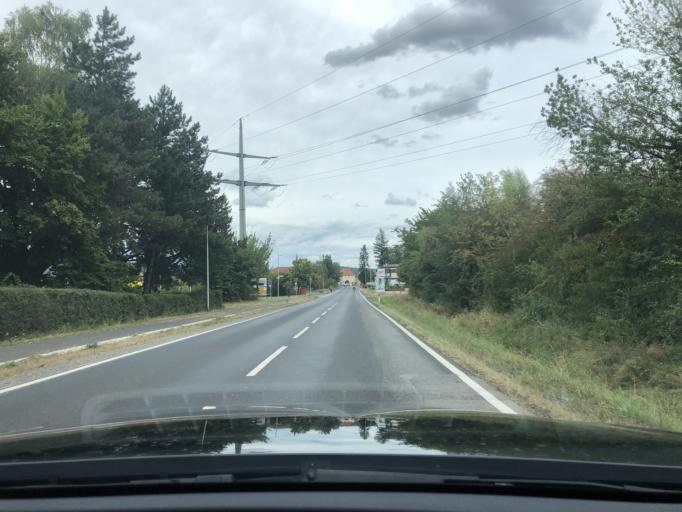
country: DE
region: Bavaria
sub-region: Regierungsbezirk Unterfranken
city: Hofheim in Unterfranken
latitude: 50.1313
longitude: 10.5206
